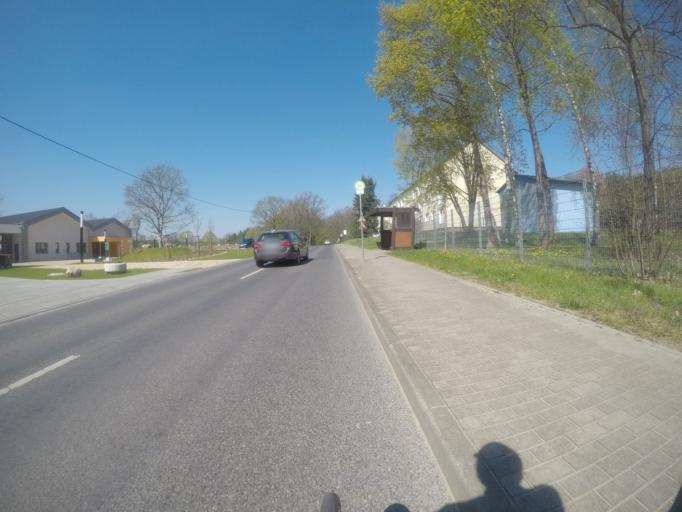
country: DE
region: Brandenburg
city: Rudnitz
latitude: 52.7567
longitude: 13.5650
